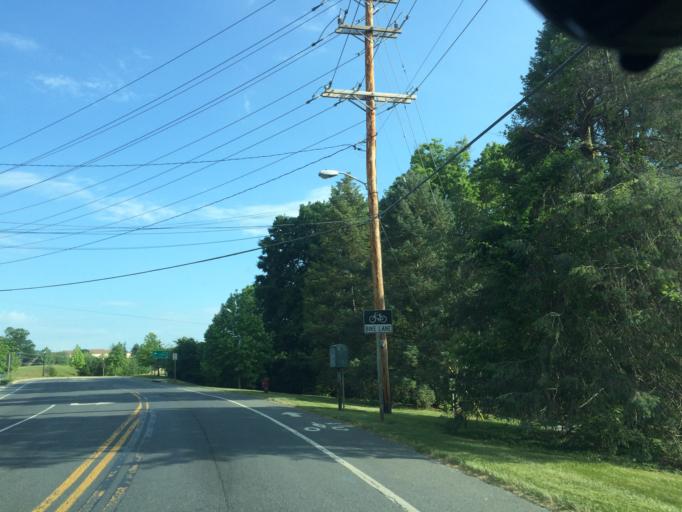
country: US
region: Maryland
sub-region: Carroll County
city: Sykesville
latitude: 39.3740
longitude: -76.9677
